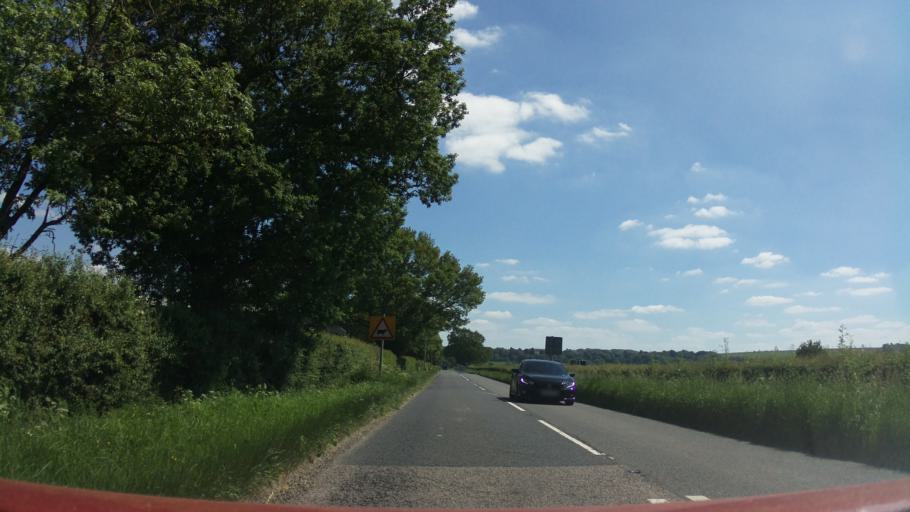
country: GB
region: England
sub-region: Borough of Swindon
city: Wroughton
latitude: 51.5369
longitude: -1.8096
